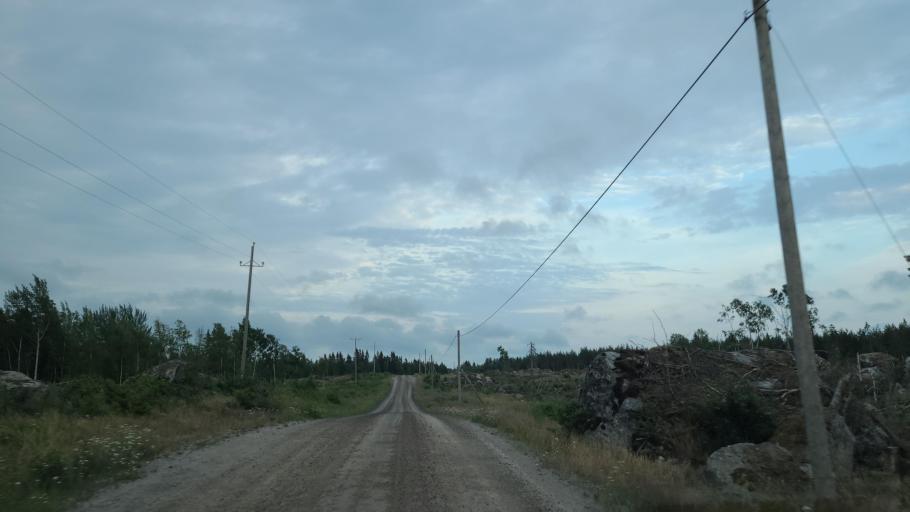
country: FI
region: Ostrobothnia
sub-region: Vaasa
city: Replot
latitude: 63.3189
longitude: 21.1485
